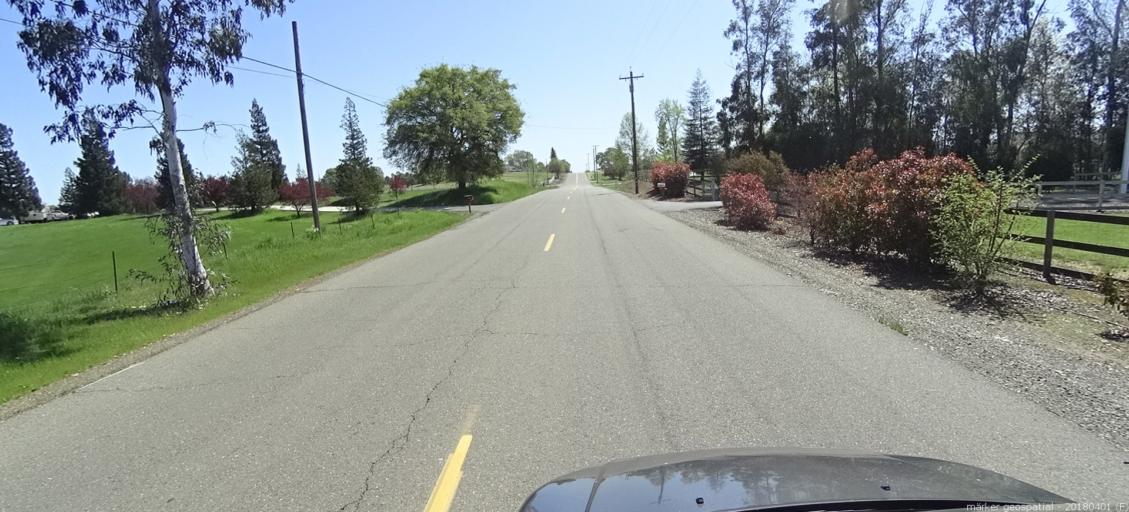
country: US
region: California
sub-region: Sacramento County
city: Wilton
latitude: 38.4210
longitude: -121.2180
